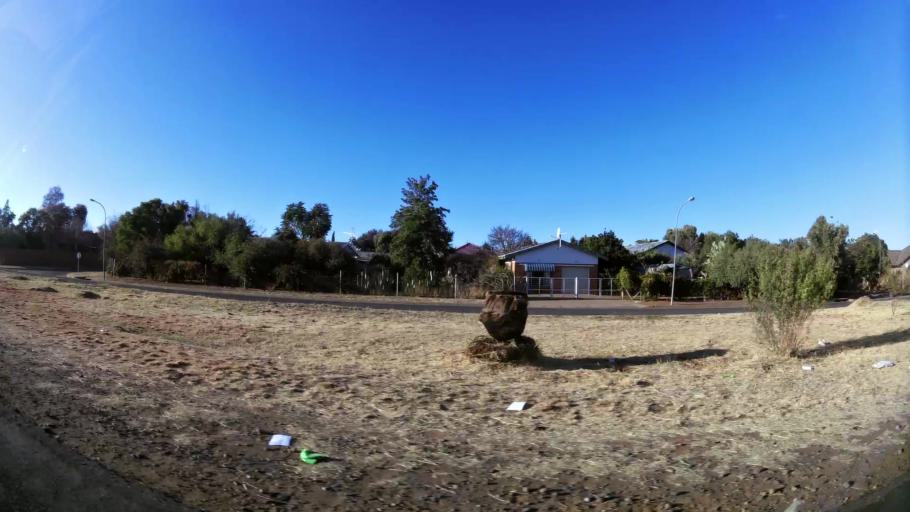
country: ZA
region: Northern Cape
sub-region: Frances Baard District Municipality
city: Kimberley
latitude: -28.7523
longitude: 24.7338
